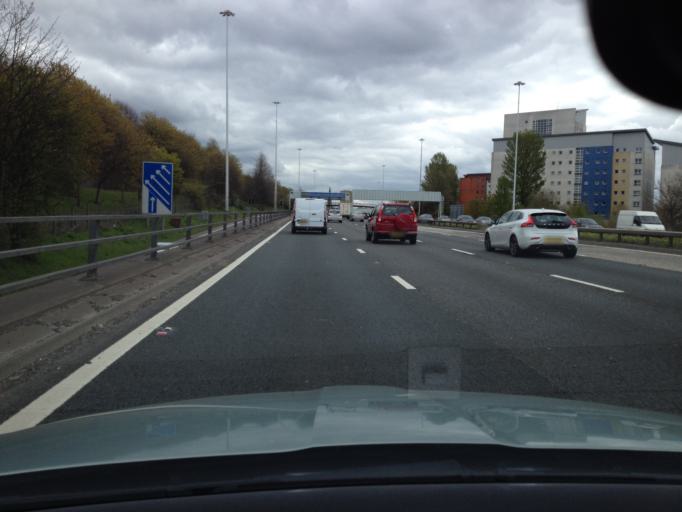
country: GB
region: Scotland
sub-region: Glasgow City
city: Glasgow
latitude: 55.8702
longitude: -4.2504
